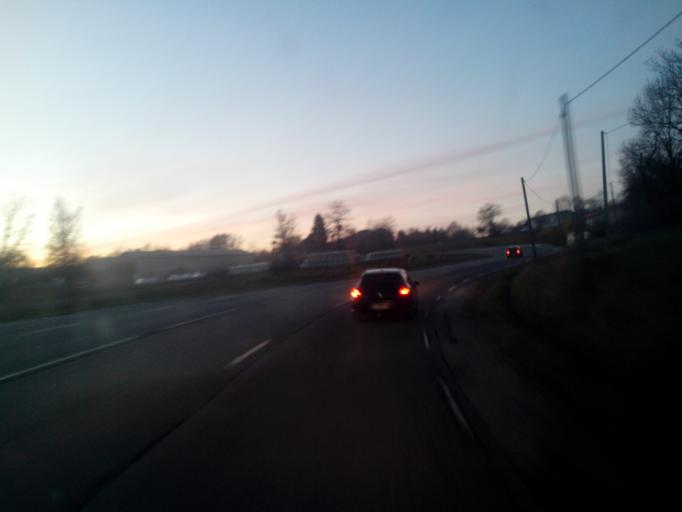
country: FR
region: Midi-Pyrenees
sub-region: Departement de l'Ariege
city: Foix
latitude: 42.9689
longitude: 1.5900
